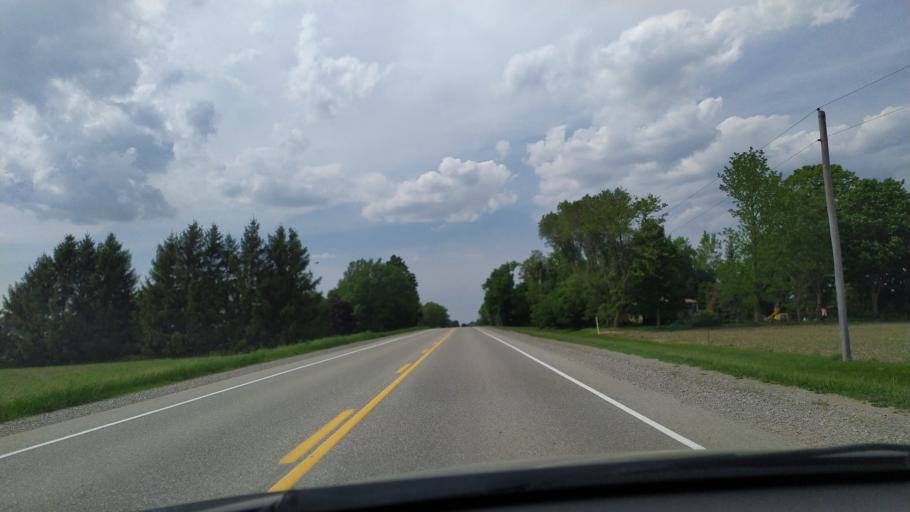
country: CA
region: Ontario
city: Dorchester
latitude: 43.1540
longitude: -81.0378
